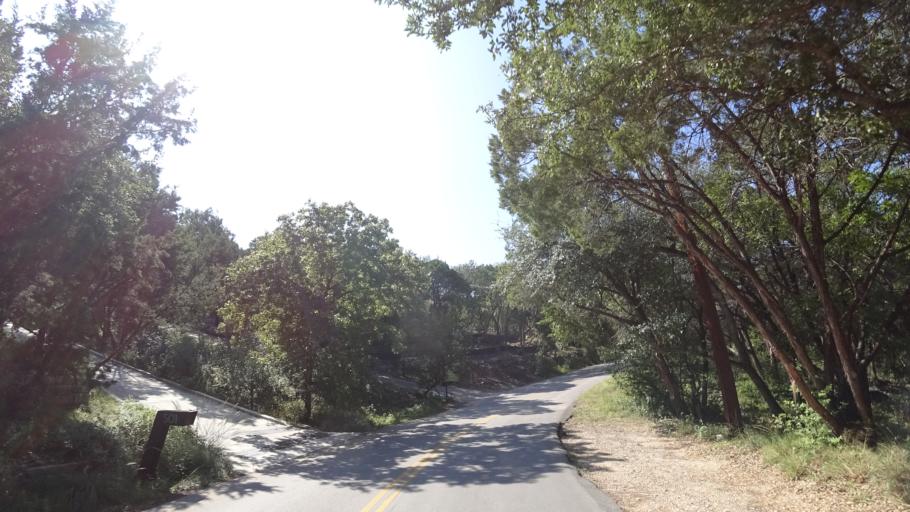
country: US
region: Texas
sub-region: Travis County
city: West Lake Hills
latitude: 30.2930
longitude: -97.8071
